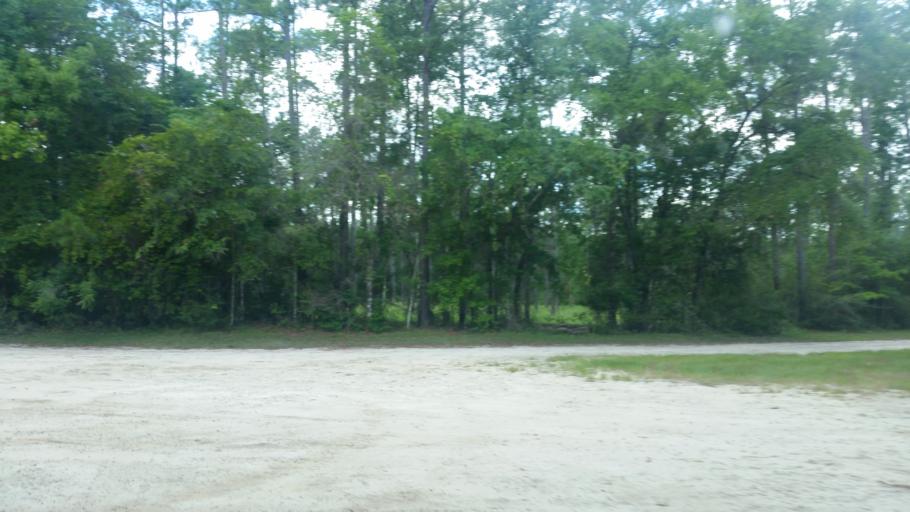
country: US
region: Florida
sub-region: Leon County
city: Woodville
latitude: 30.2849
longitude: -84.1530
